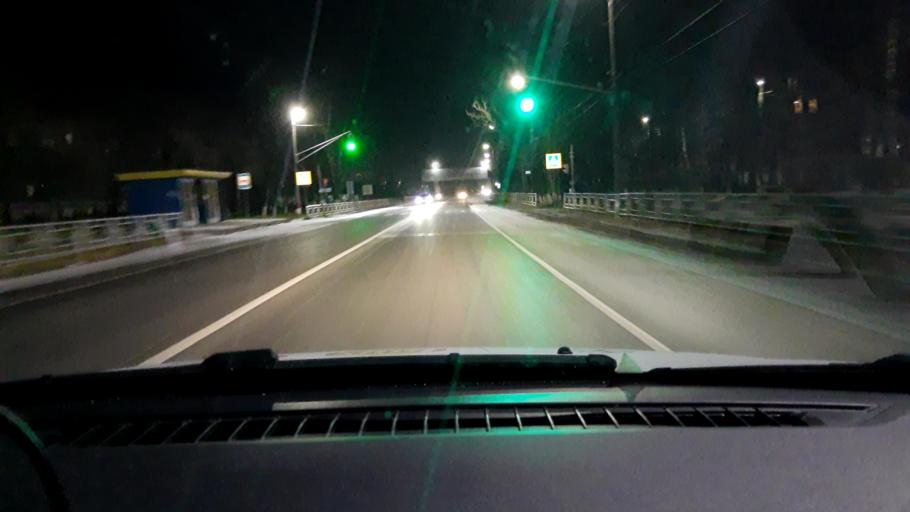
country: RU
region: Nizjnij Novgorod
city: Novaya Balakhna
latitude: 56.5224
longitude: 43.5667
